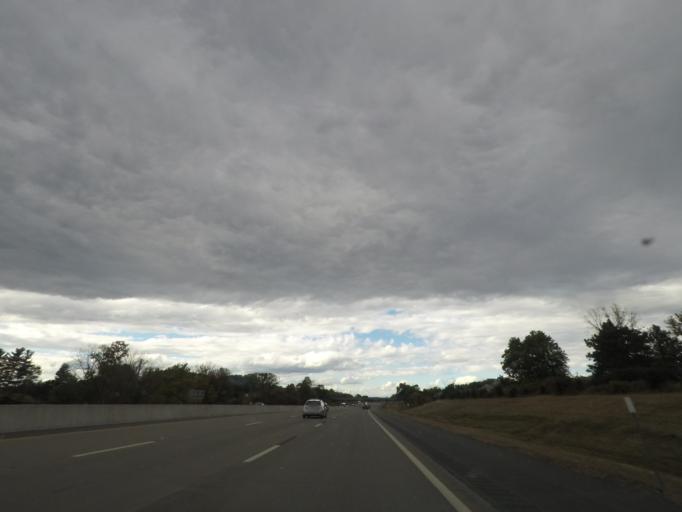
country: US
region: New York
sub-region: Albany County
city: Delmar
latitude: 42.6511
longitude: -73.8155
